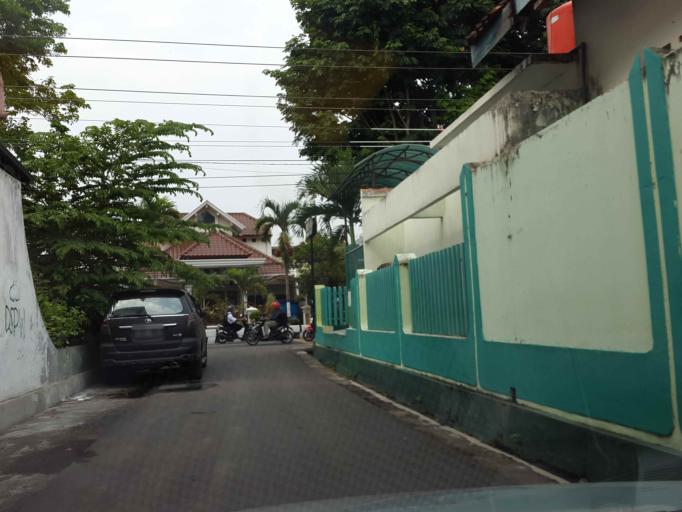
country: ID
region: Central Java
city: Jaten
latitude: -7.5987
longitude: 110.9560
